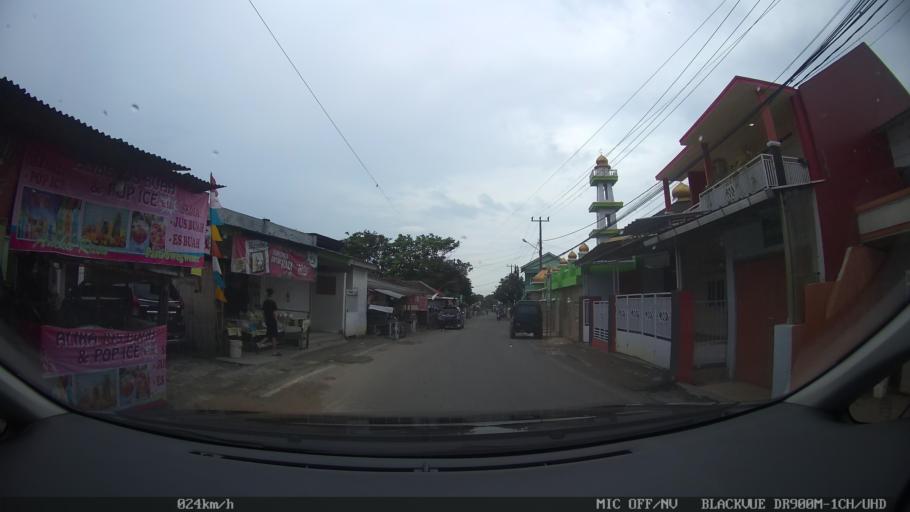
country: ID
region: Lampung
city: Kedaton
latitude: -5.3816
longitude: 105.2486
